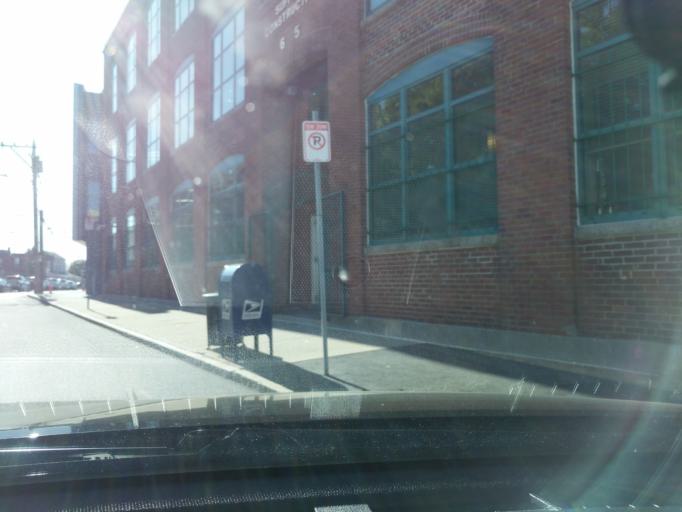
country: US
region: Massachusetts
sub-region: Suffolk County
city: South Boston
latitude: 42.3285
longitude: -71.0701
